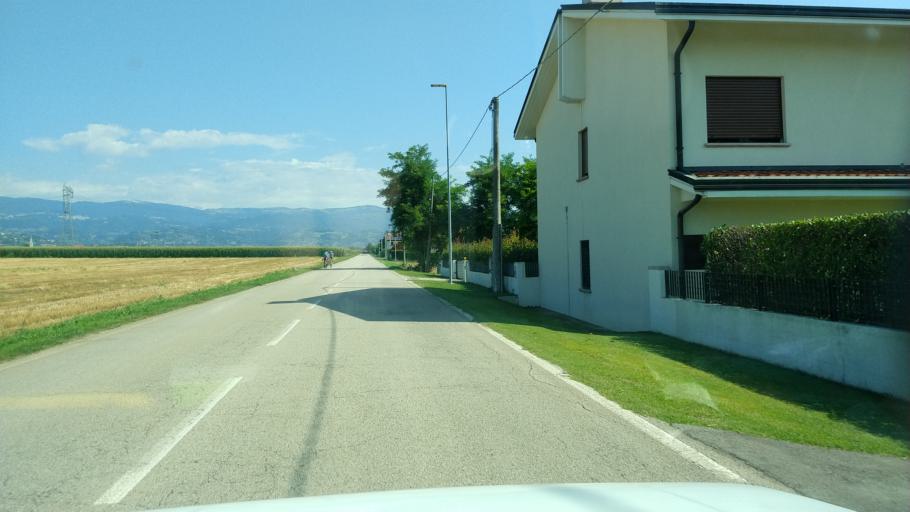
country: IT
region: Veneto
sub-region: Provincia di Vicenza
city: Sandrigo
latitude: 45.6745
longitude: 11.6087
